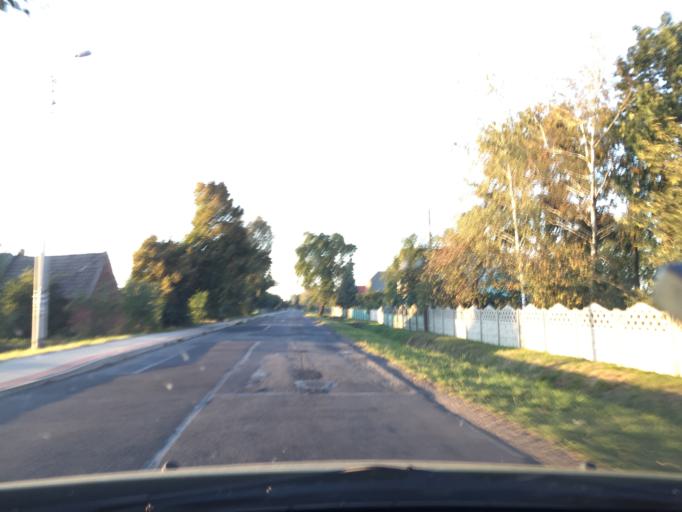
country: PL
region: Greater Poland Voivodeship
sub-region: Powiat pleszewski
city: Dobrzyca
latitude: 51.8151
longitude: 17.6219
